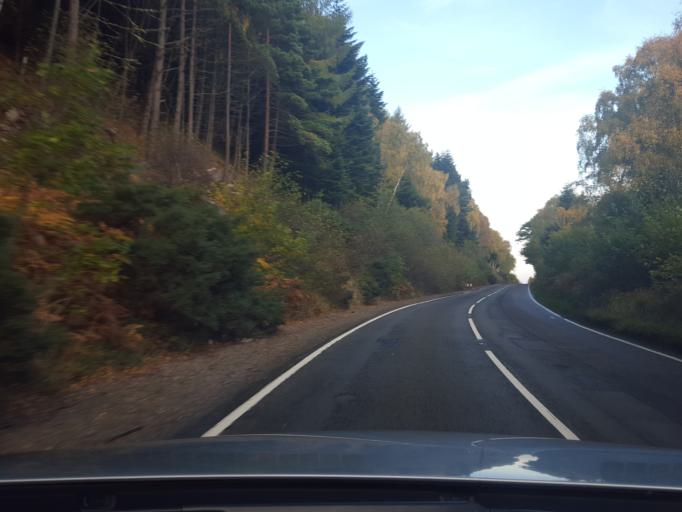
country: GB
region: Scotland
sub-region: Highland
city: Beauly
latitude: 57.3543
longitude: -4.4052
